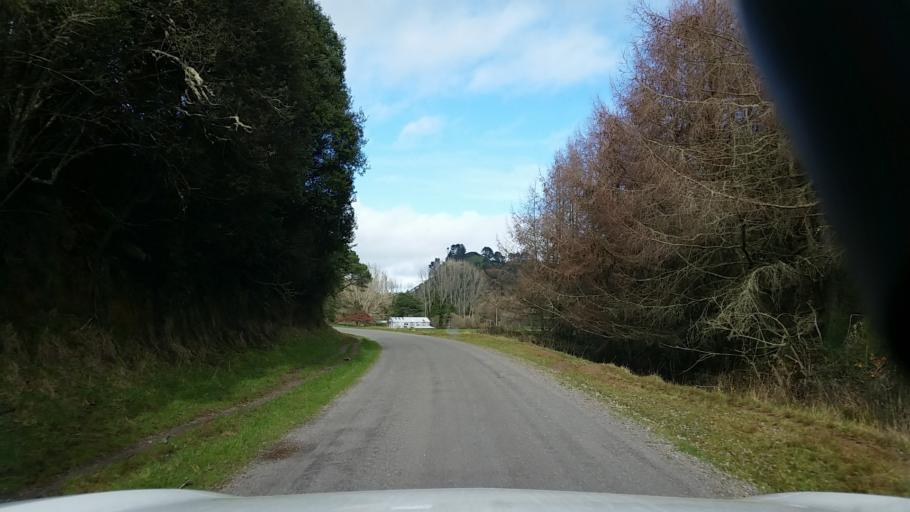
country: NZ
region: Waikato
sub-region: Taupo District
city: Taupo
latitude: -38.4600
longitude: 176.2409
